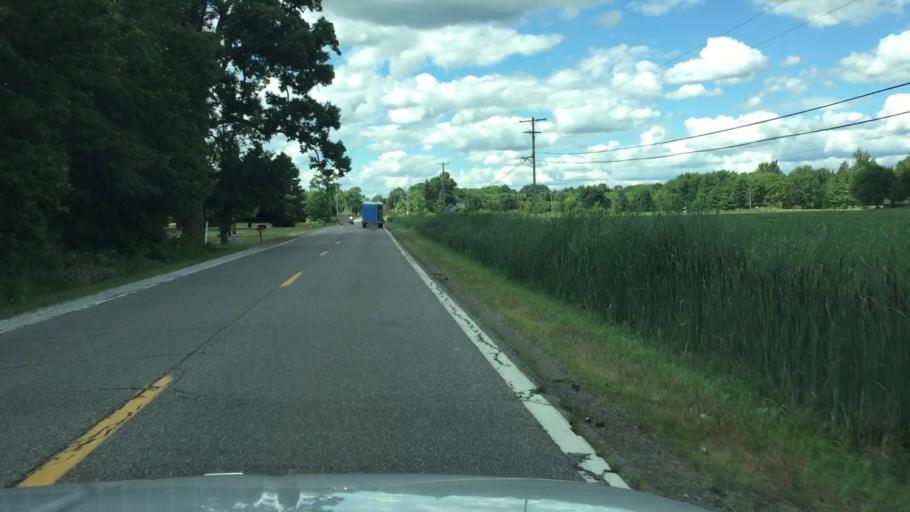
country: US
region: Michigan
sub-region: Macomb County
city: Armada
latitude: 42.8830
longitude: -82.9455
